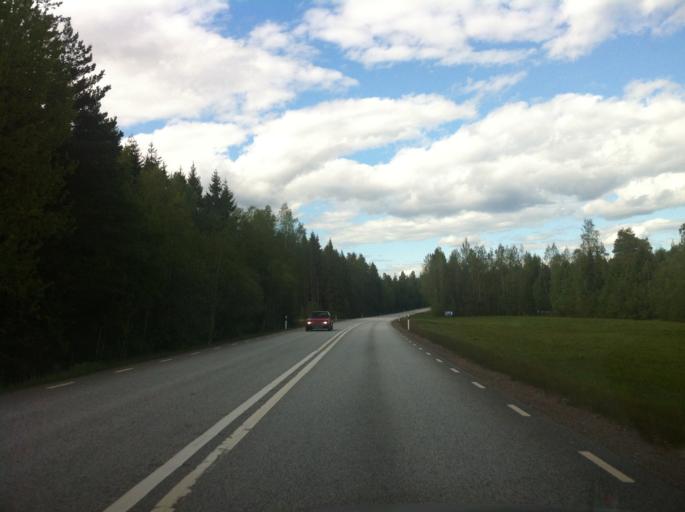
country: SE
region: Vaermland
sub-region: Storfors Kommun
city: Storfors
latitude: 59.5171
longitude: 14.2696
